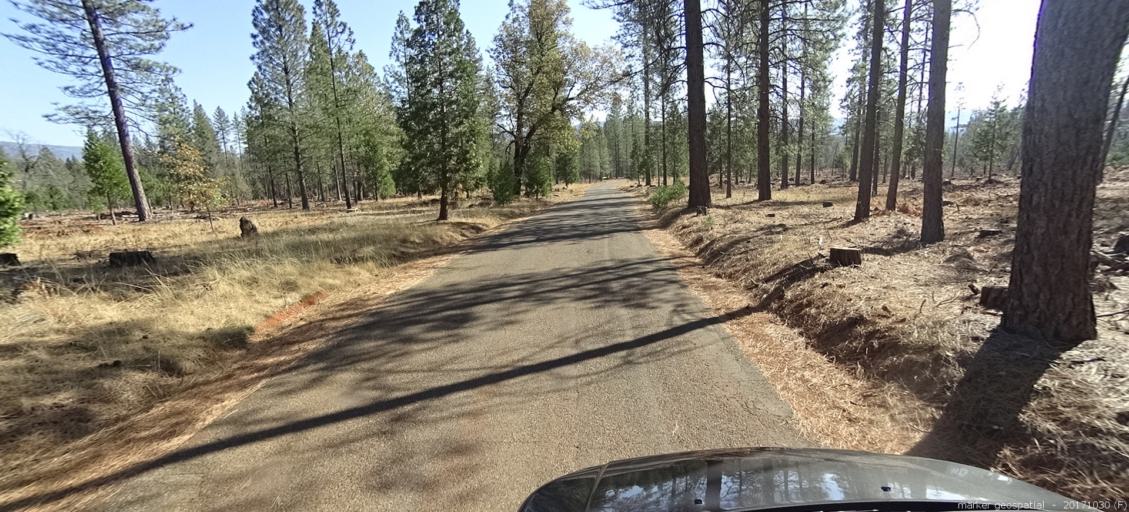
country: US
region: California
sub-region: Shasta County
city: Shingletown
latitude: 40.6101
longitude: -121.8651
